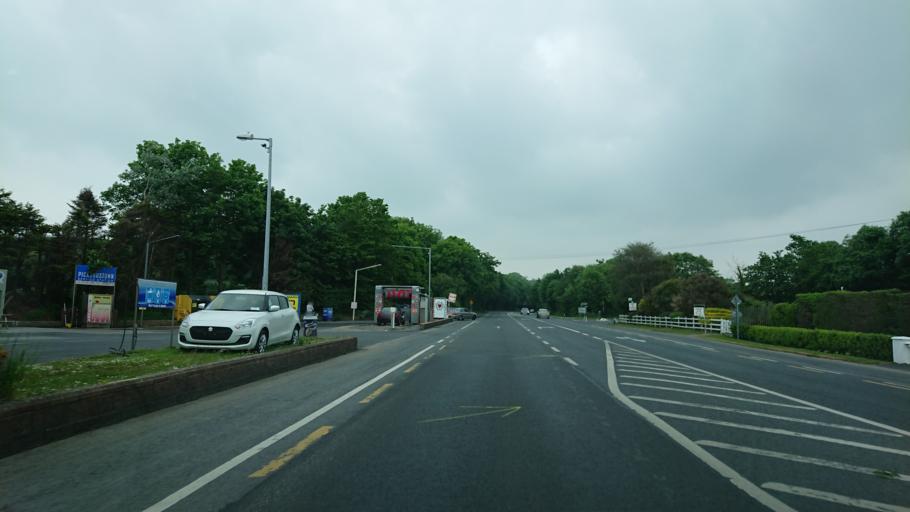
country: IE
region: Munster
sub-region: Waterford
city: Tra Mhor
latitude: 52.1756
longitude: -7.1378
